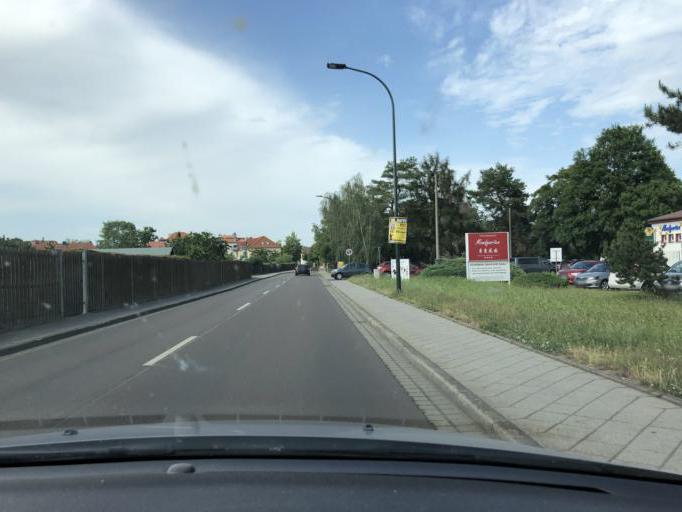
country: DE
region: Saxony
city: Markkleeberg
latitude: 51.2739
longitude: 12.3772
